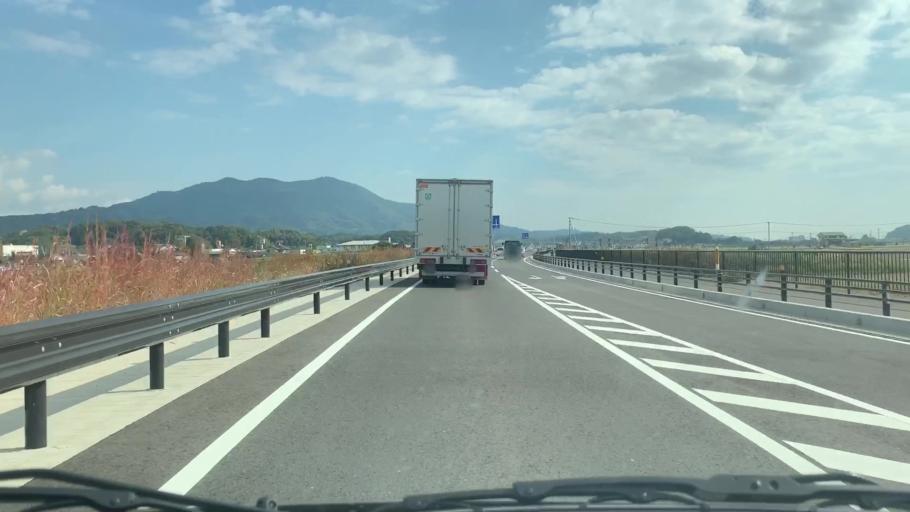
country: JP
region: Saga Prefecture
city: Takeocho-takeo
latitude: 33.2176
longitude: 130.0565
